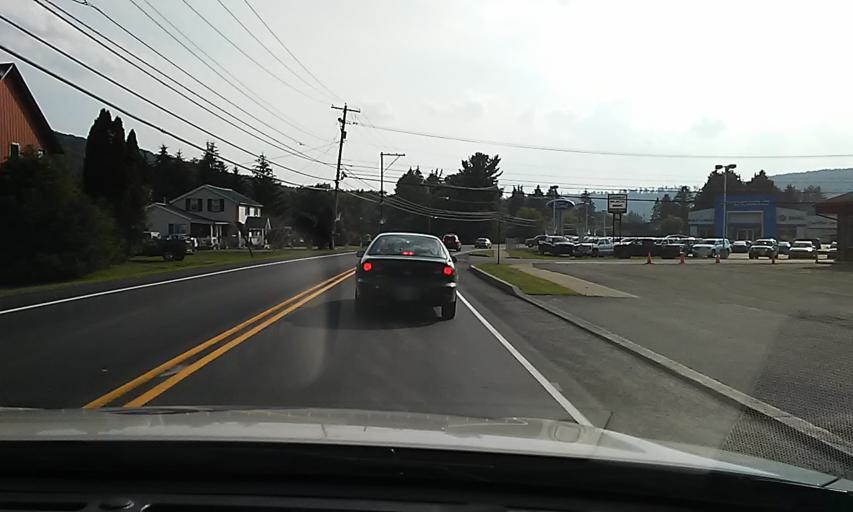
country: US
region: Pennsylvania
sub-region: Potter County
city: Coudersport
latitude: 41.7645
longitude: -78.0337
